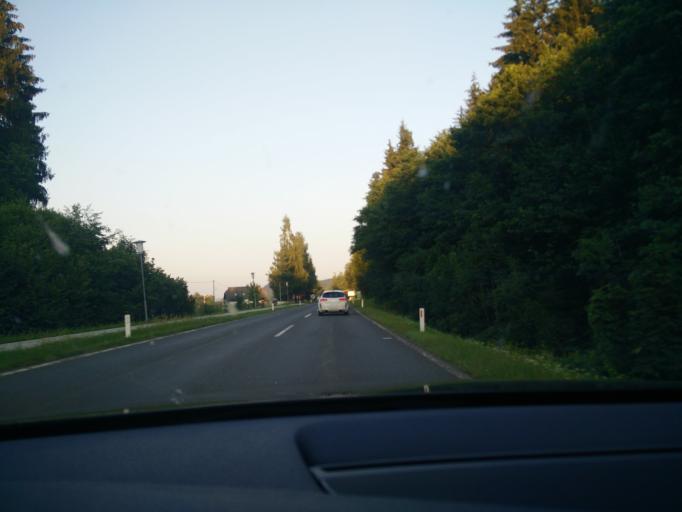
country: AT
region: Carinthia
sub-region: Politischer Bezirk Villach Land
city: Wernberg
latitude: 46.5893
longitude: 13.9050
